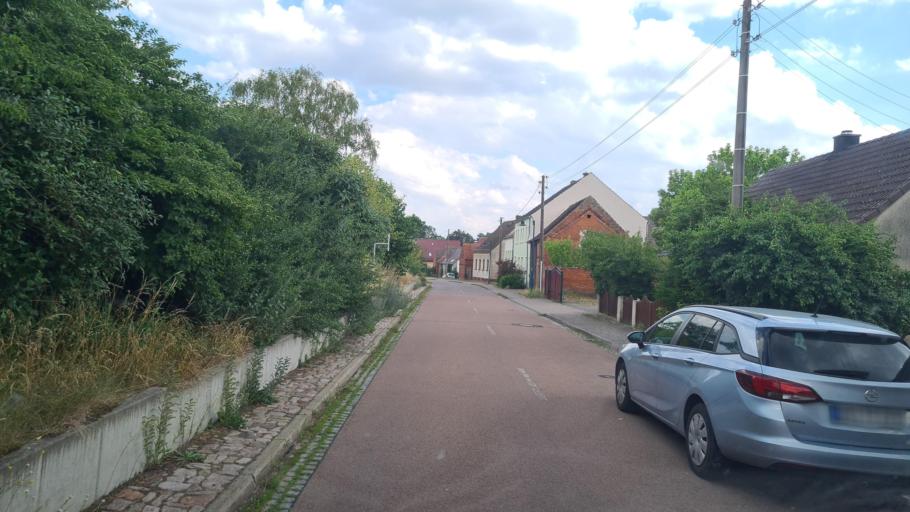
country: DE
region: Saxony-Anhalt
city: Kropstadt
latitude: 51.9514
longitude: 12.6994
